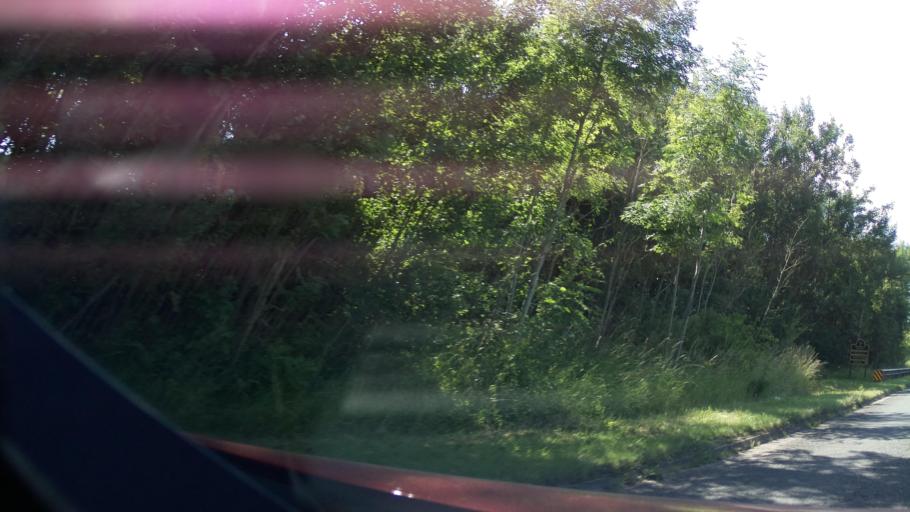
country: GB
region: England
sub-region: Worcestershire
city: Redditch
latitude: 52.3075
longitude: -1.9814
